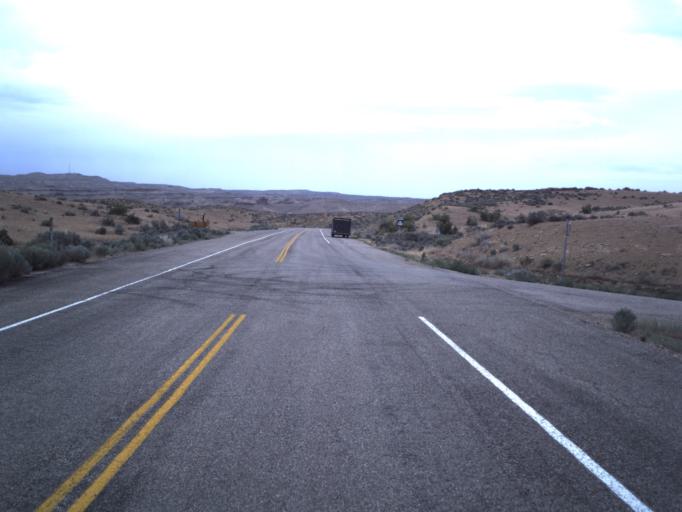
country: US
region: Colorado
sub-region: Rio Blanco County
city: Rangely
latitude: 39.9585
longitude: -109.1634
